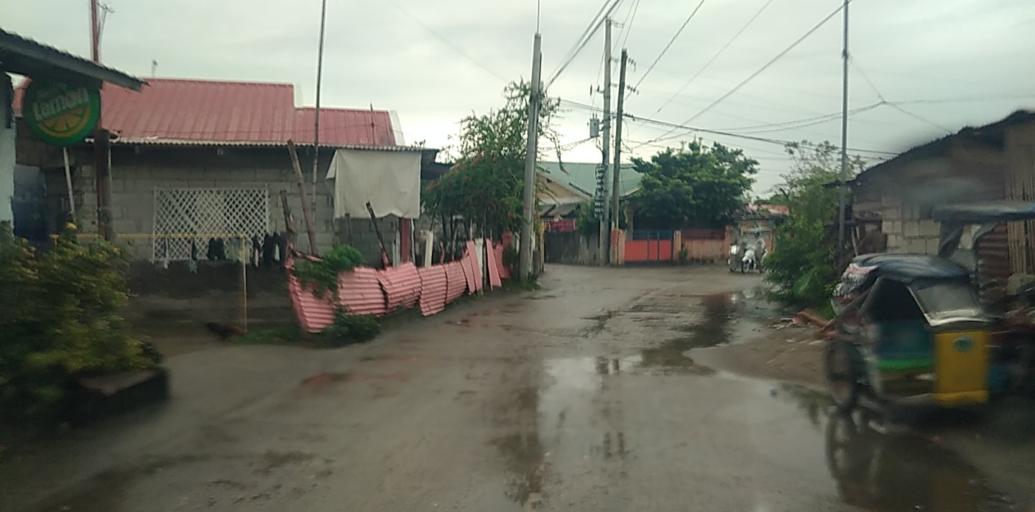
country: PH
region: Central Luzon
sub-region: Province of Pampanga
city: Arayat
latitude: 15.1353
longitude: 120.7421
